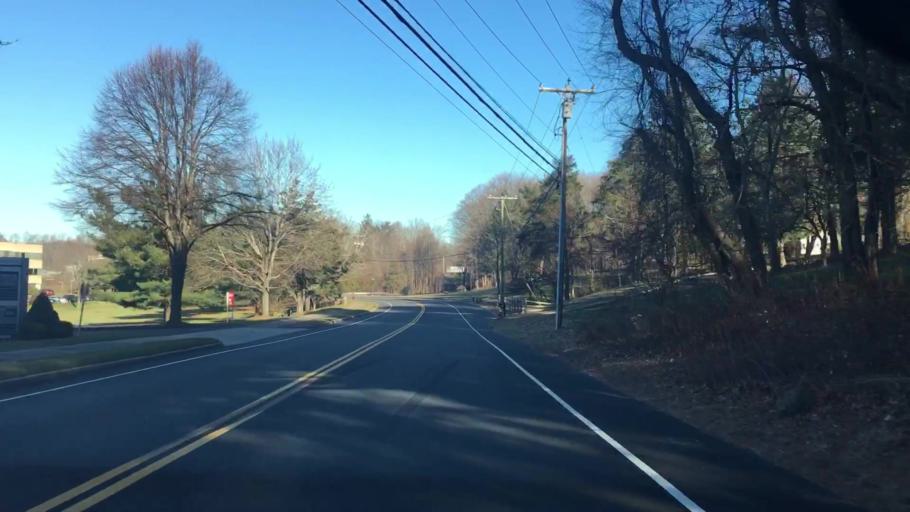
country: US
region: Connecticut
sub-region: New Haven County
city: Meriden
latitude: 41.5404
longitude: -72.7515
